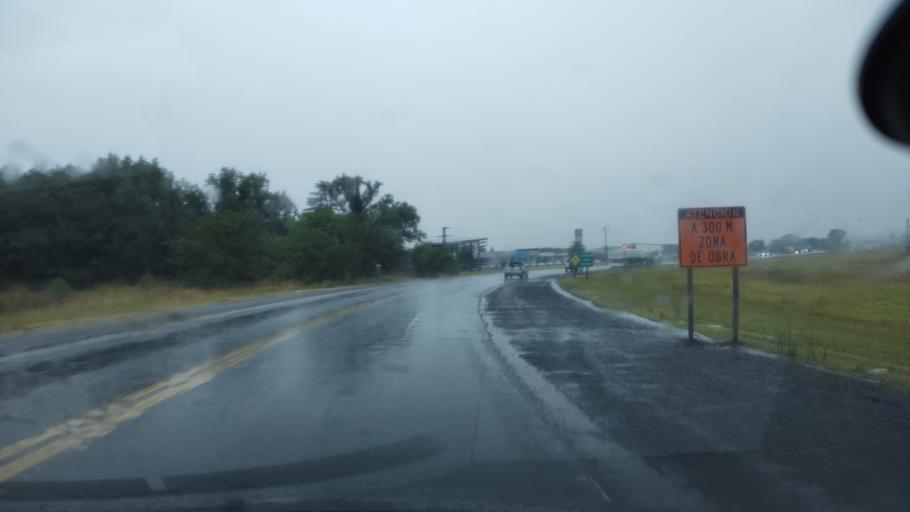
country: AR
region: Buenos Aires
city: Canuelas
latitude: -35.0244
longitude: -58.7469
